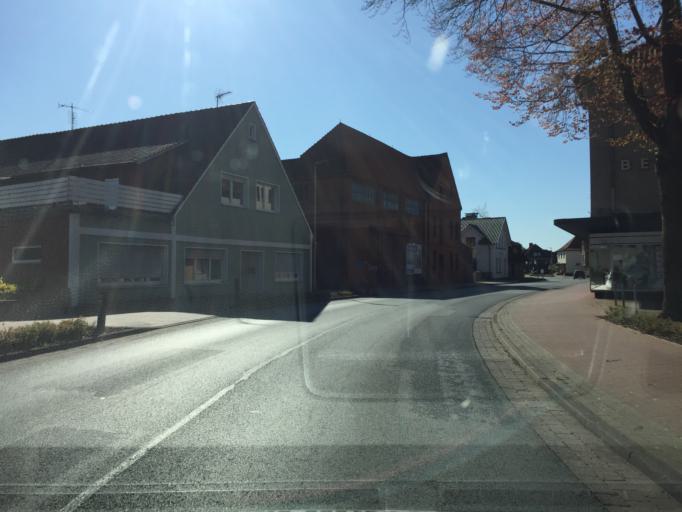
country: DE
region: Lower Saxony
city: Wagenfeld
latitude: 52.5496
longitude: 8.5879
